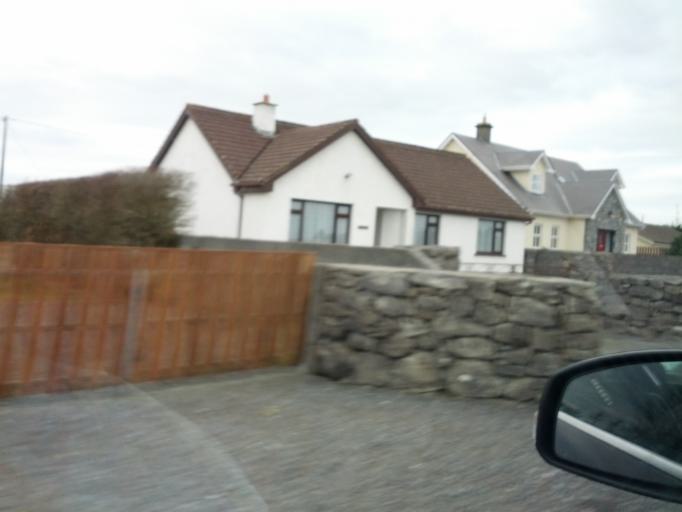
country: IE
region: Connaught
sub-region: County Galway
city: Oranmore
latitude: 53.2502
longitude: -8.8451
